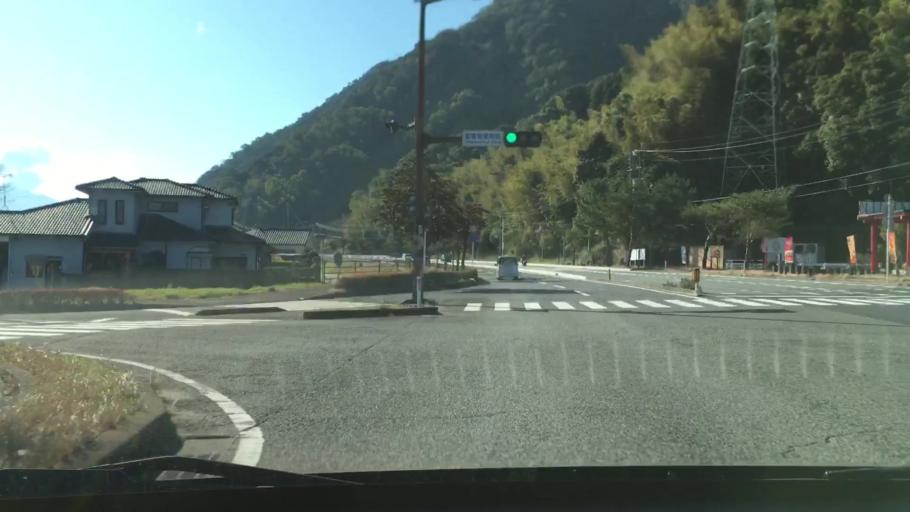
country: JP
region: Kagoshima
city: Kajiki
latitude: 31.7031
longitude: 130.6117
